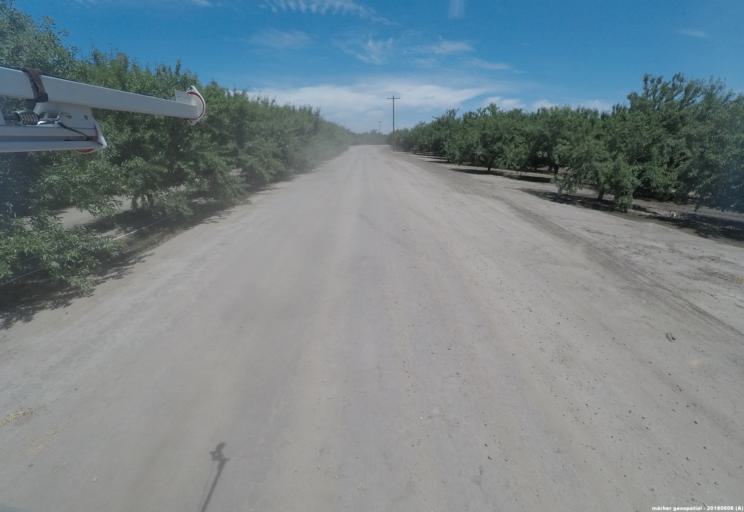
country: US
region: California
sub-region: Fresno County
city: Mendota
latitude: 36.8217
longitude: -120.3701
